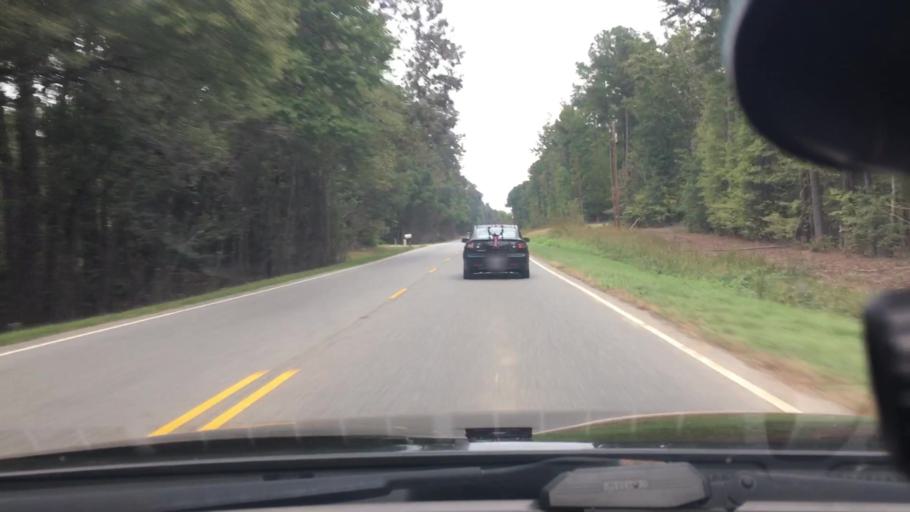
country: US
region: North Carolina
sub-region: Moore County
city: Robbins
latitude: 35.3844
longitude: -79.6554
